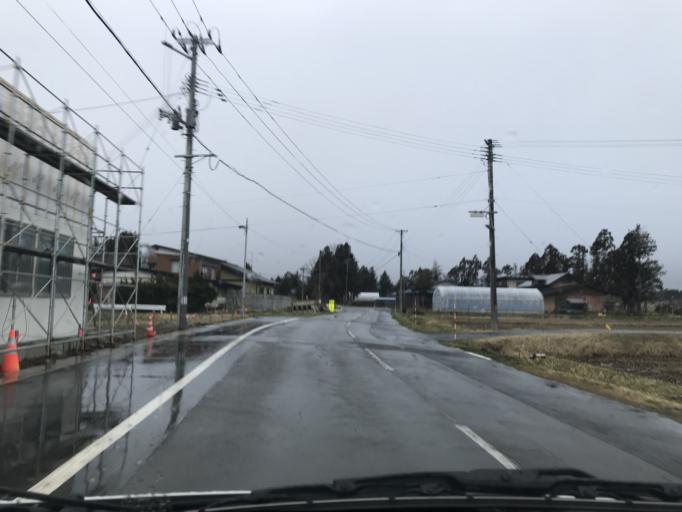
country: JP
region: Iwate
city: Kitakami
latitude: 39.2259
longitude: 141.0870
